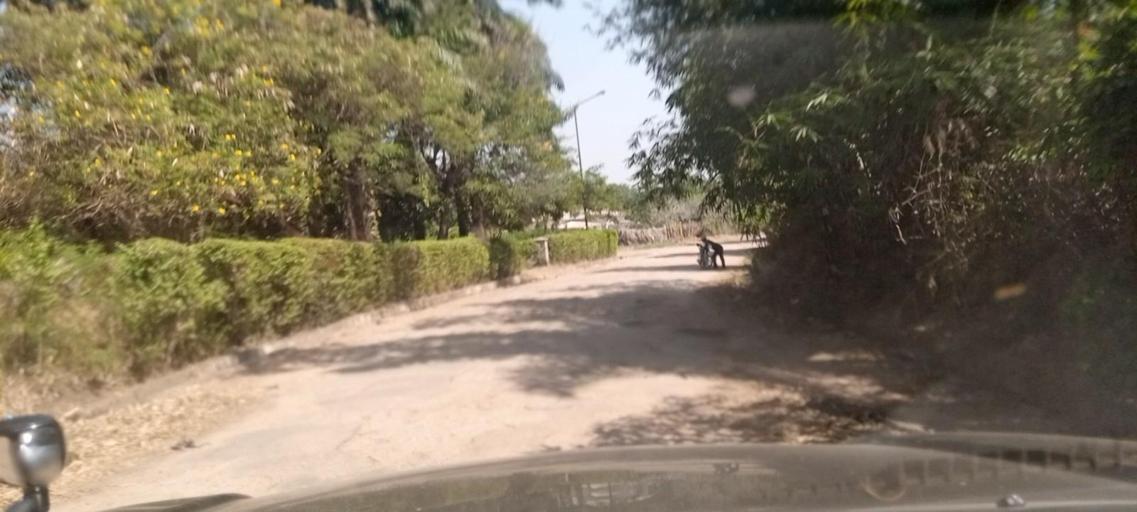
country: CD
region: Kasai-Oriental
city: Mbuji-Mayi
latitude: -6.1231
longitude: 23.5888
